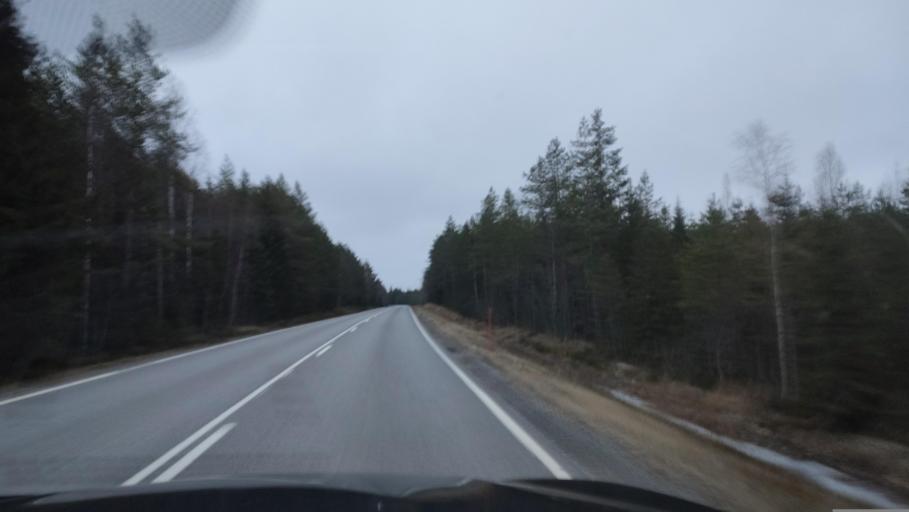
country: FI
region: Southern Ostrobothnia
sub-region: Suupohja
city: Isojoki
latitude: 62.3385
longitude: 21.9368
